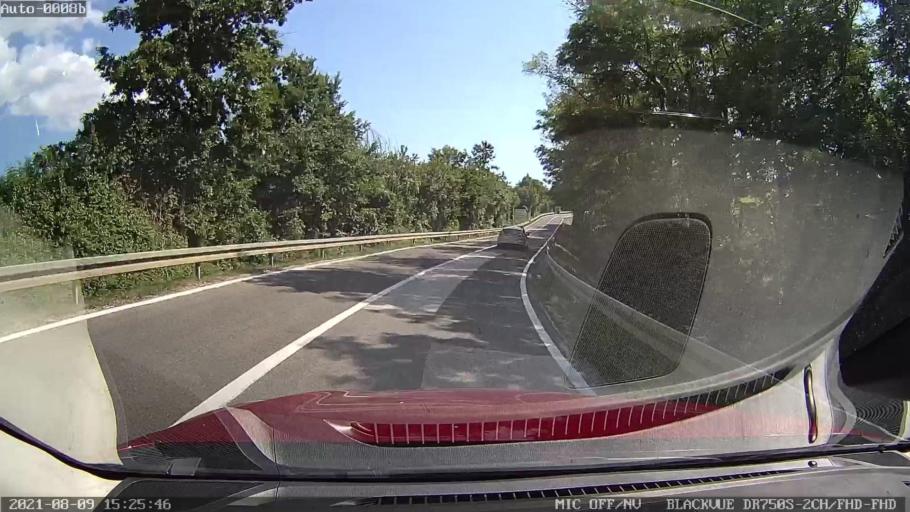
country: HR
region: Istarska
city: Pazin
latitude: 45.1668
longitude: 13.9091
